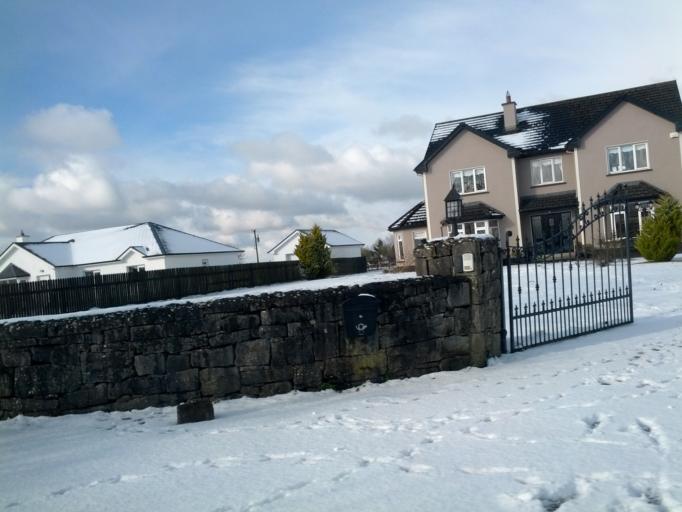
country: IE
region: Connaught
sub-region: County Galway
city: Athenry
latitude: 53.2148
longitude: -8.7613
